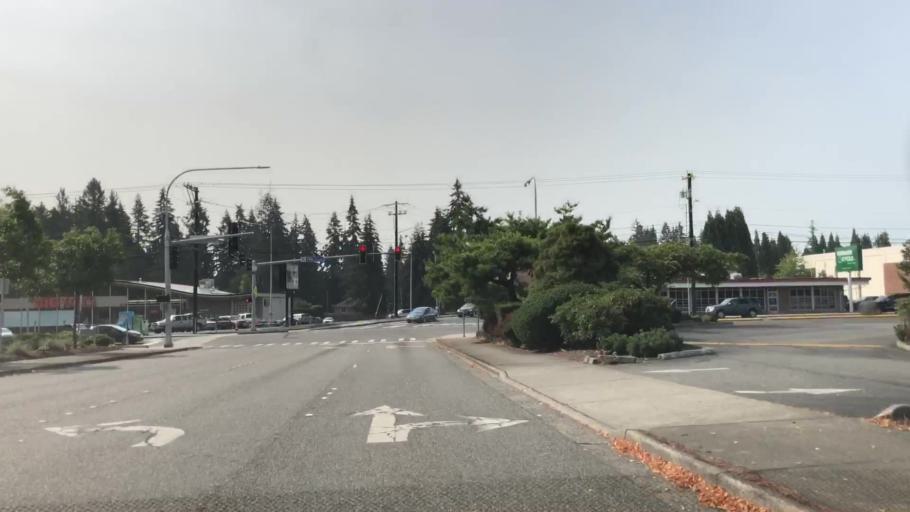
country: US
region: Washington
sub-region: Snohomish County
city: Lynnwood
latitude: 47.8216
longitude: -122.3110
